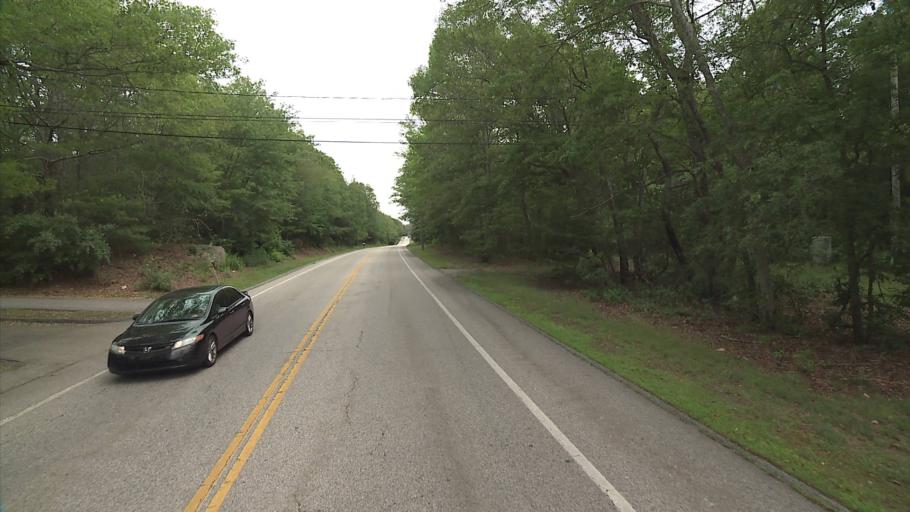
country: US
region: Connecticut
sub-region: New London County
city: Poquonock Bridge
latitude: 41.3734
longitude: -72.0267
